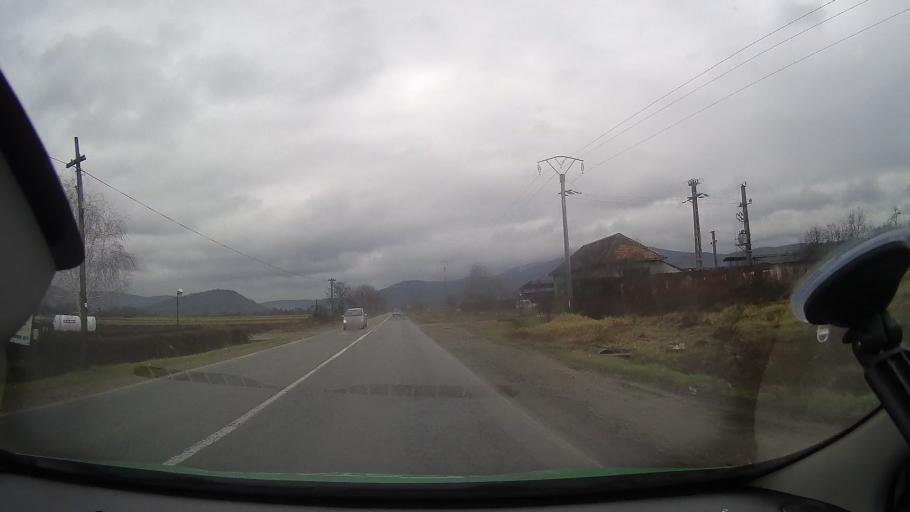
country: RO
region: Arad
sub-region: Comuna Buteni
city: Buteni
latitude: 46.3212
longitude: 22.1298
